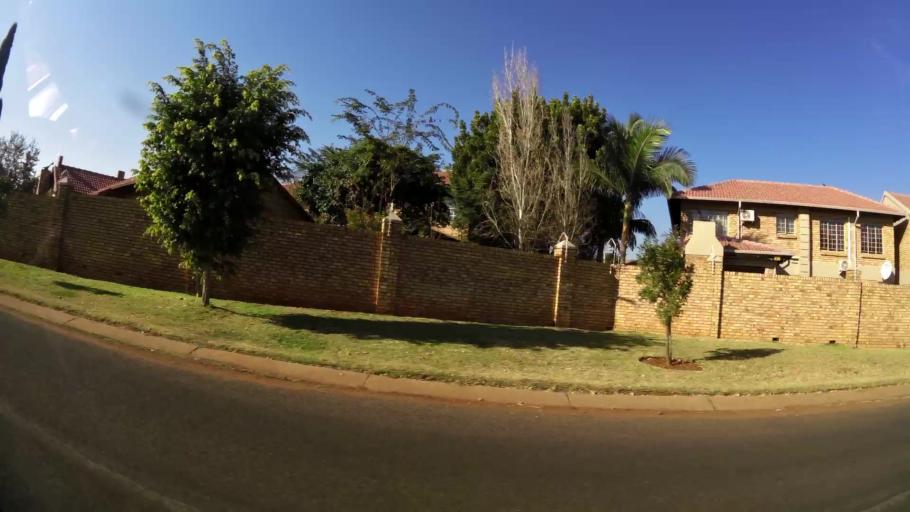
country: ZA
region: Gauteng
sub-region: City of Tshwane Metropolitan Municipality
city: Pretoria
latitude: -25.6777
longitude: 28.2264
